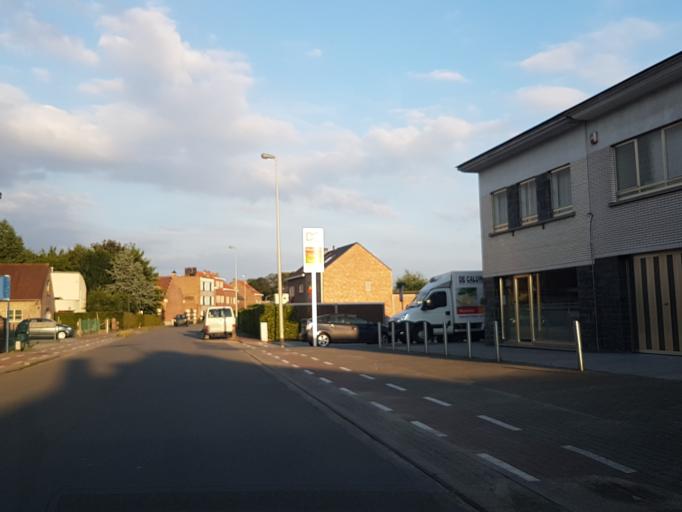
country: BE
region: Flanders
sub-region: Provincie Vlaams-Brabant
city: Dilbeek
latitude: 50.8447
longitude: 4.2378
